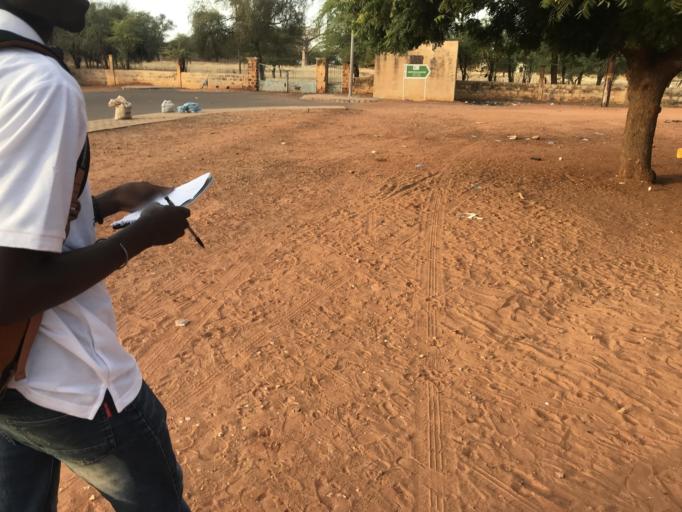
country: SN
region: Louga
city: Ndibene Dahra
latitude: 15.4010
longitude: -15.1127
